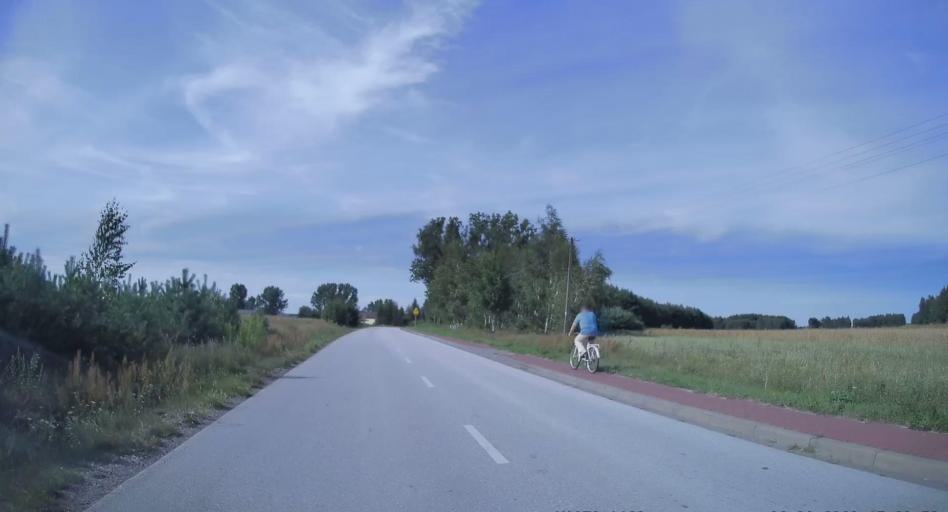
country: PL
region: Lodz Voivodeship
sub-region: Powiat opoczynski
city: Mniszkow
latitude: 51.3465
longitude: 20.0382
